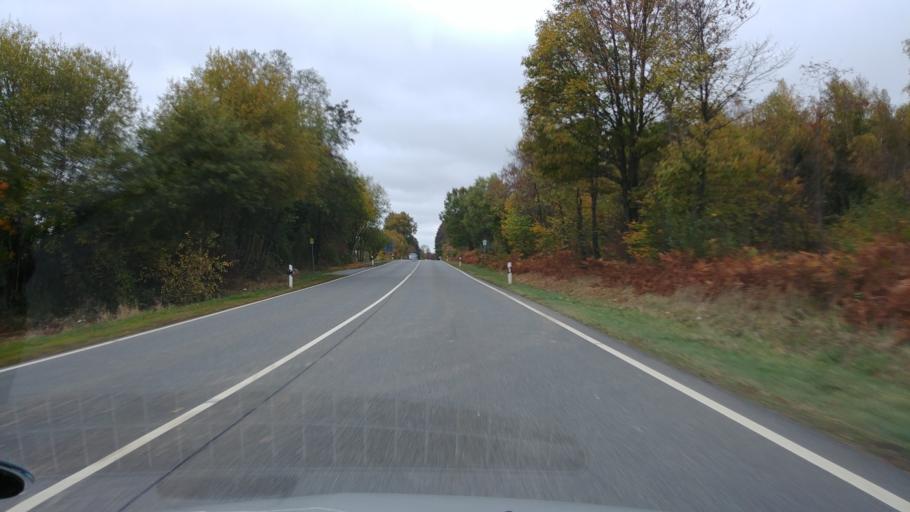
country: DE
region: Rheinland-Pfalz
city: Malborn
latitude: 49.6919
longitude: 6.9756
